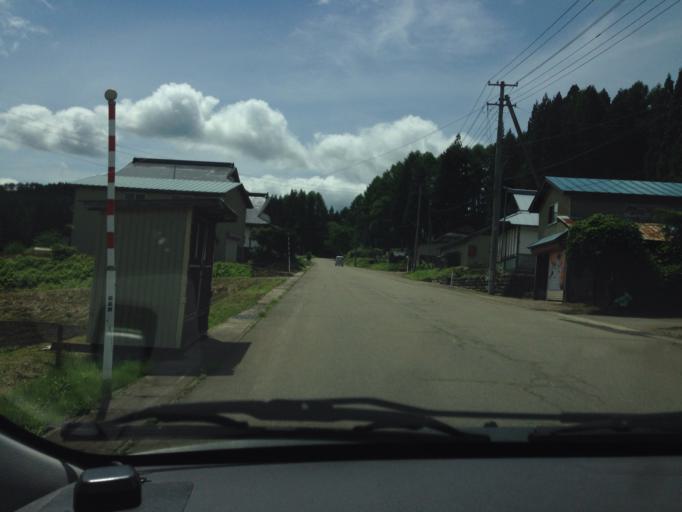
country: JP
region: Fukushima
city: Kitakata
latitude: 37.2910
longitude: 139.8451
